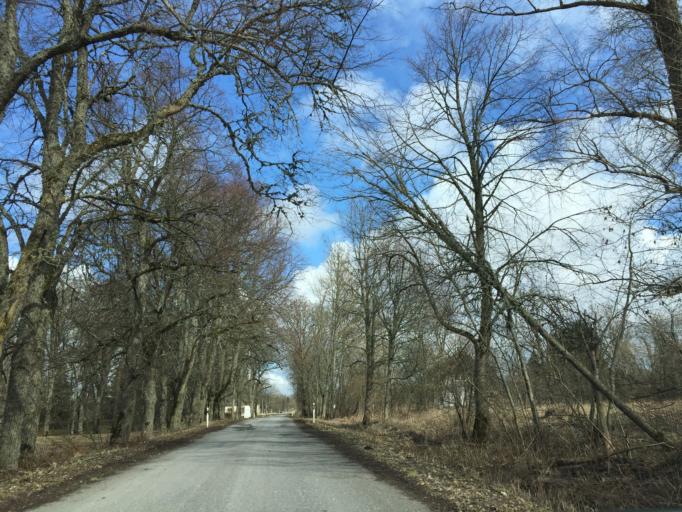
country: EE
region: Laeaene
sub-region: Lihula vald
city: Lihula
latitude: 58.7131
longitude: 23.8155
